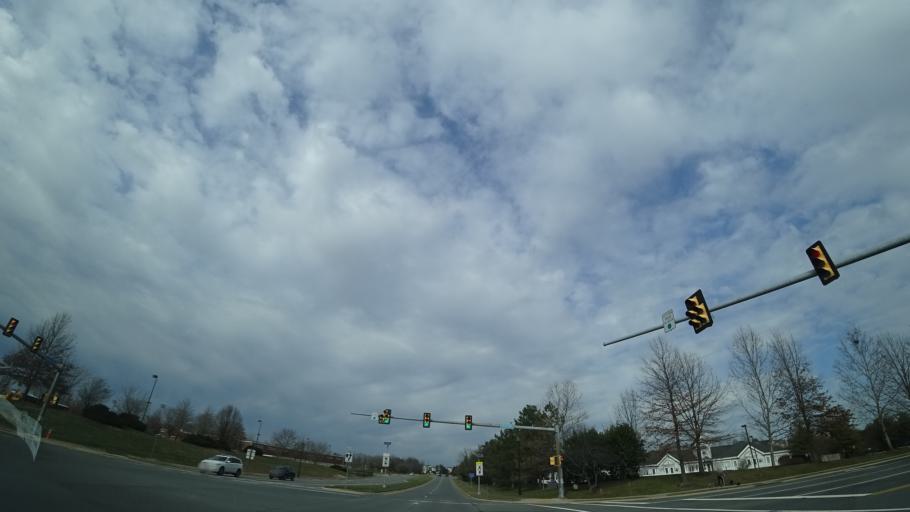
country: US
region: Virginia
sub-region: Loudoun County
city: Belmont
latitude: 39.0459
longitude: -77.5076
